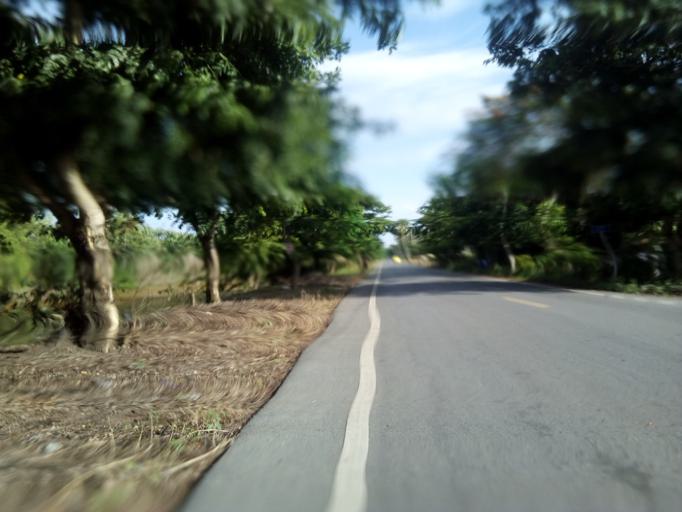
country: TH
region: Pathum Thani
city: Nong Suea
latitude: 14.1308
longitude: 100.8459
